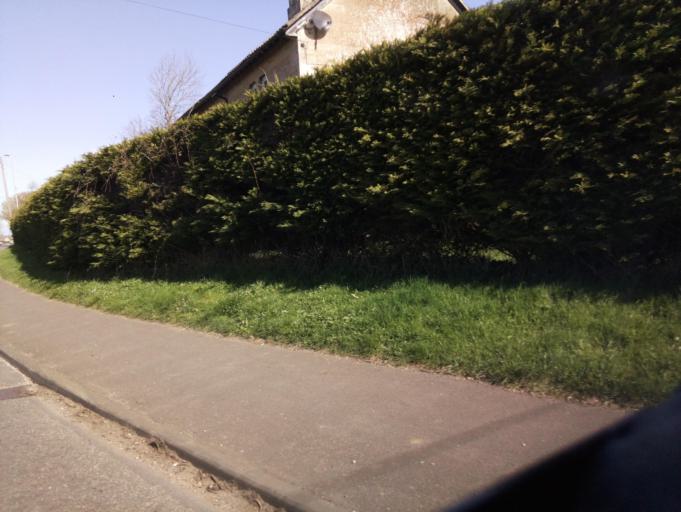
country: GB
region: England
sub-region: Wiltshire
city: Bradford-on-Avon
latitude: 51.3333
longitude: -2.2371
